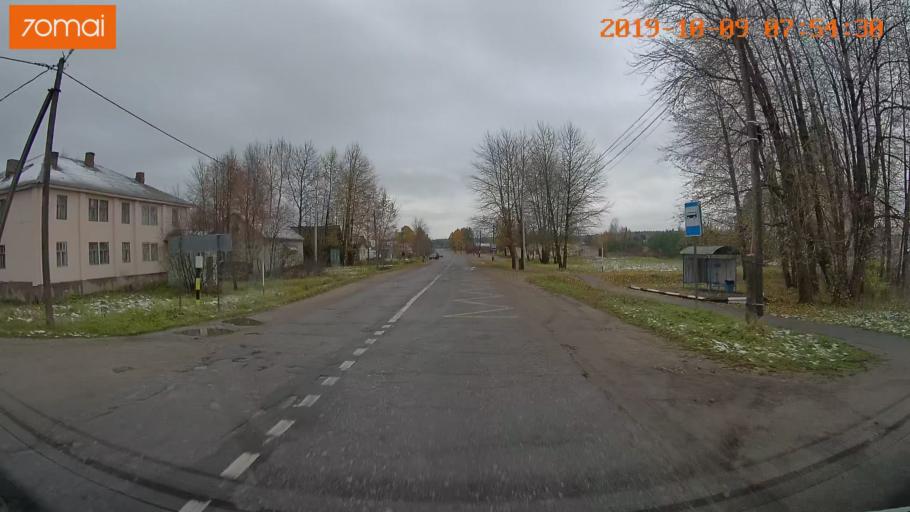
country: RU
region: Jaroslavl
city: Kukoboy
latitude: 58.6988
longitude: 39.9083
